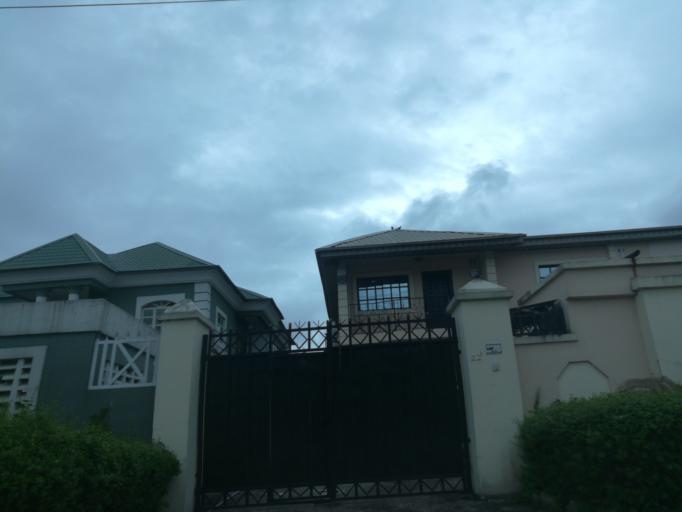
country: NG
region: Lagos
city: Ikoyi
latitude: 6.4400
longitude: 3.4684
